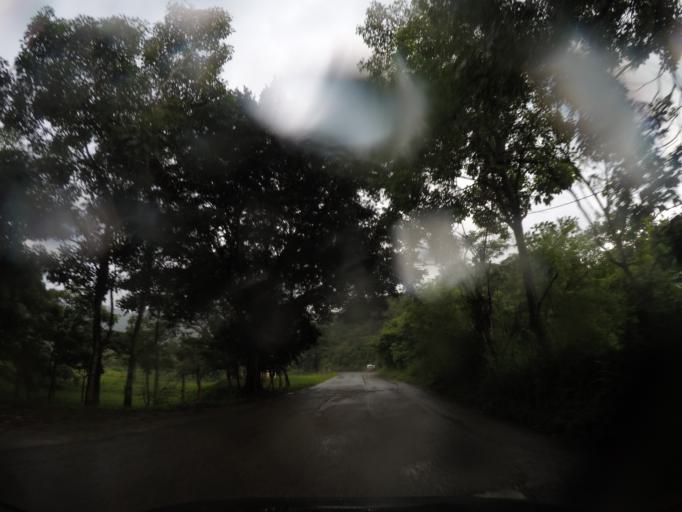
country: MX
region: Oaxaca
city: San Gabriel Mixtepec
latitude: 16.1091
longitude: -97.0661
